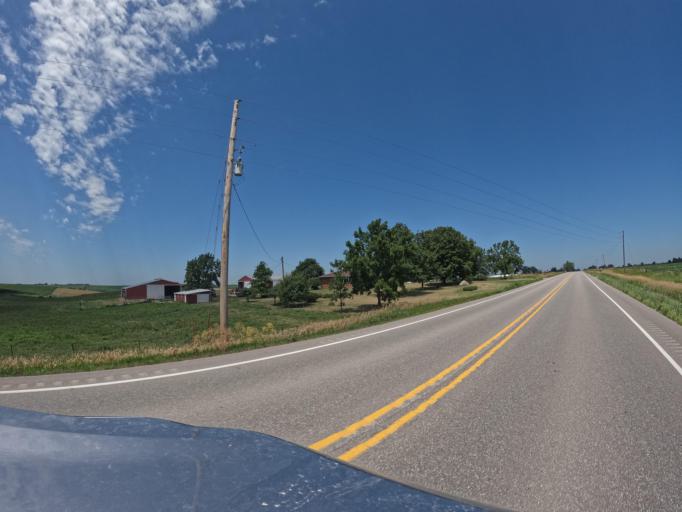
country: US
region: Iowa
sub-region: Keokuk County
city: Sigourney
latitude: 41.4309
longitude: -92.3549
